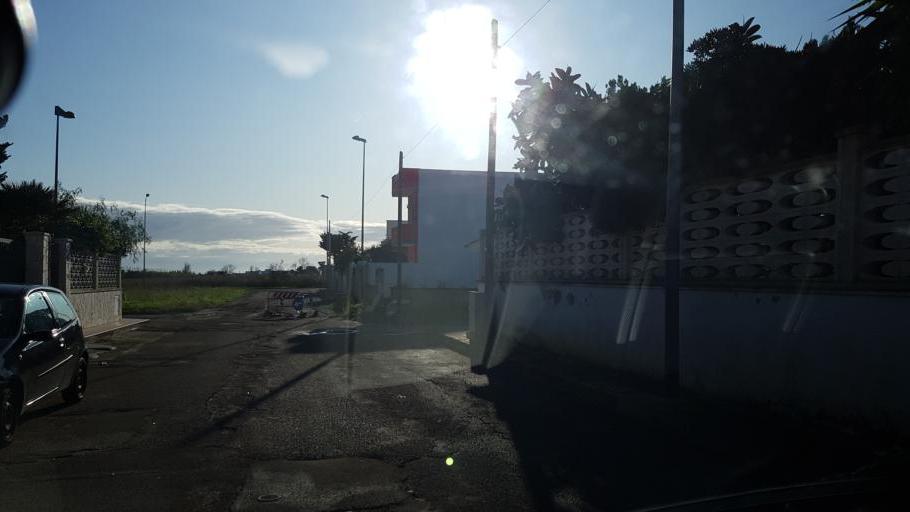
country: IT
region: Apulia
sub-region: Provincia di Brindisi
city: Torchiarolo
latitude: 40.5344
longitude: 18.0714
